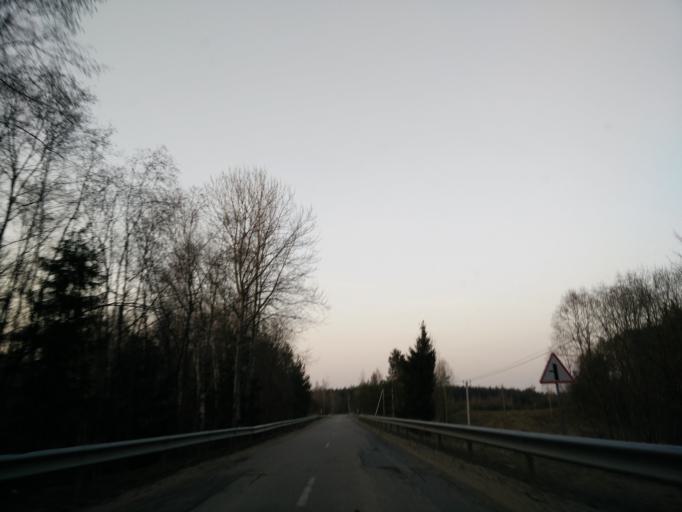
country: LT
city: Trakai
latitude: 54.7109
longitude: 24.9698
